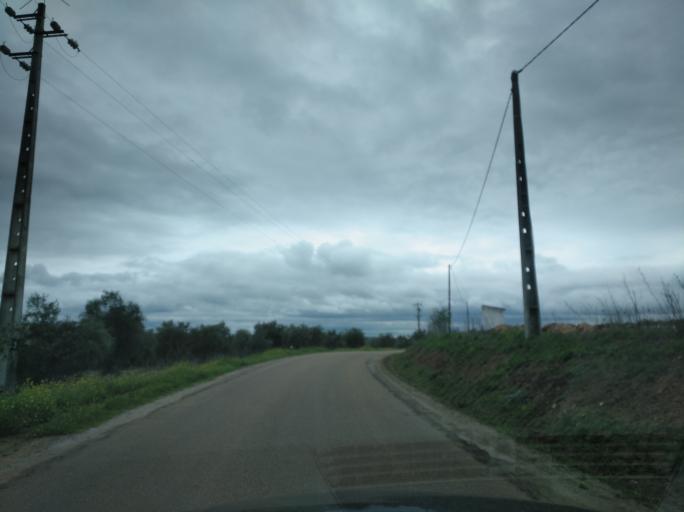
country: PT
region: Portalegre
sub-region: Campo Maior
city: Campo Maior
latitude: 38.9924
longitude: -7.0522
